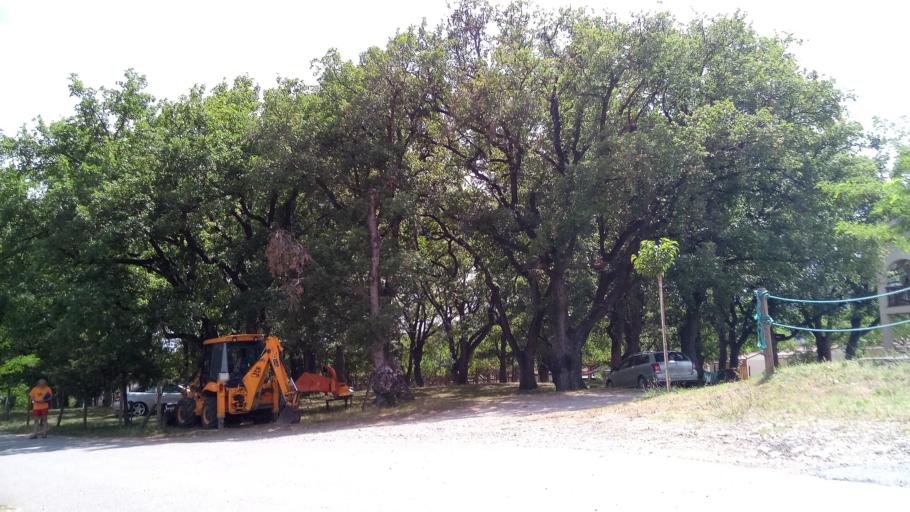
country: ES
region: Aragon
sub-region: Provincia de Huesca
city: Castigaleu
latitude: 42.3098
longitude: 0.5443
